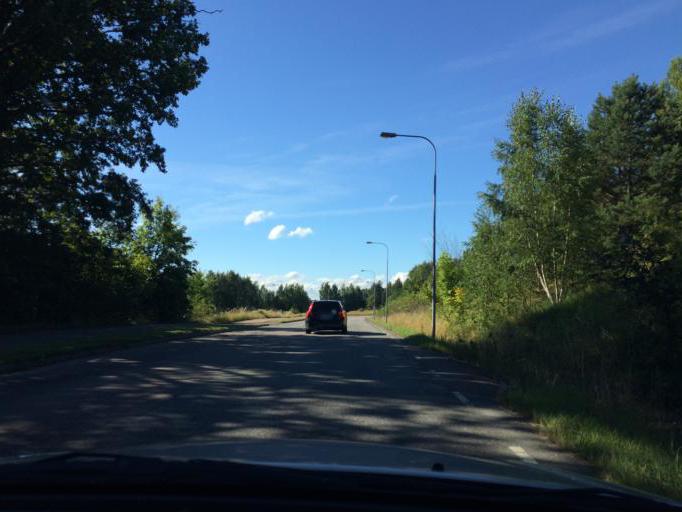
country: SE
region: Vaestmanland
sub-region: Vasteras
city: Hokasen
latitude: 59.6052
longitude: 16.6288
